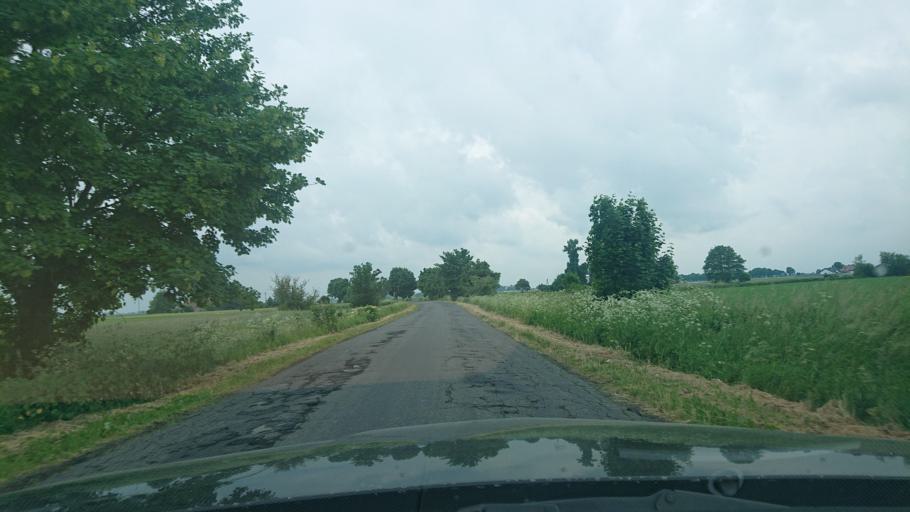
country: PL
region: Greater Poland Voivodeship
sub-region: Powiat gnieznienski
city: Czerniejewo
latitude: 52.4507
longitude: 17.5535
